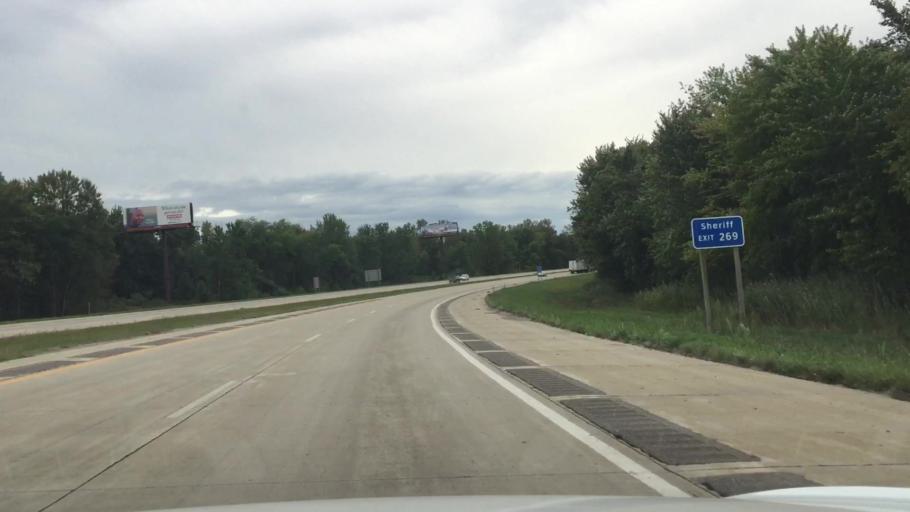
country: US
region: Michigan
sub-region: Saint Clair County
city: Marysville
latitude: 42.9593
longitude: -82.4901
